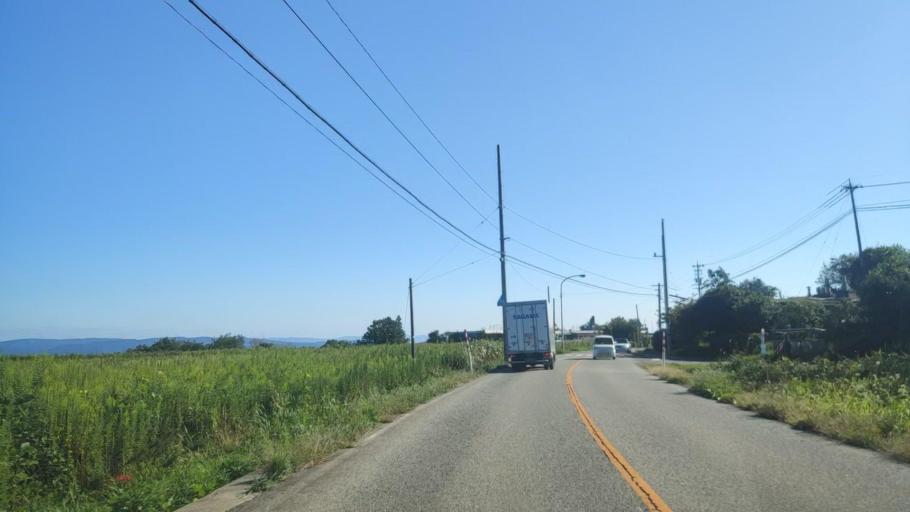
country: JP
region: Ishikawa
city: Nanao
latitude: 37.1947
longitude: 136.9109
